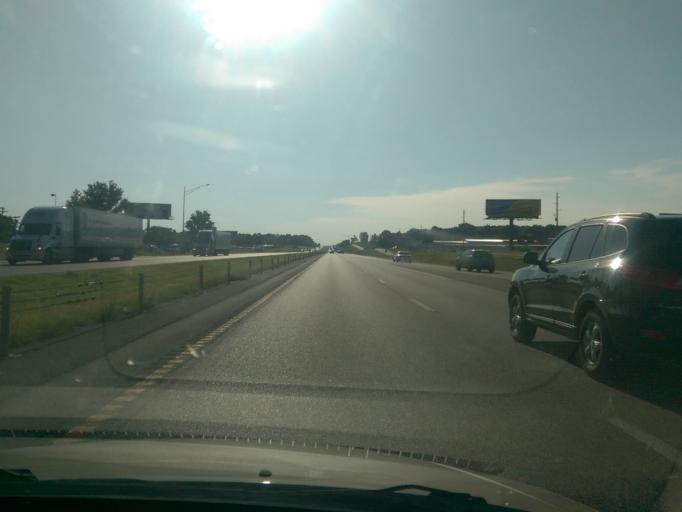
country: US
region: Missouri
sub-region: Jackson County
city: Grain Valley
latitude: 39.0218
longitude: -94.2006
